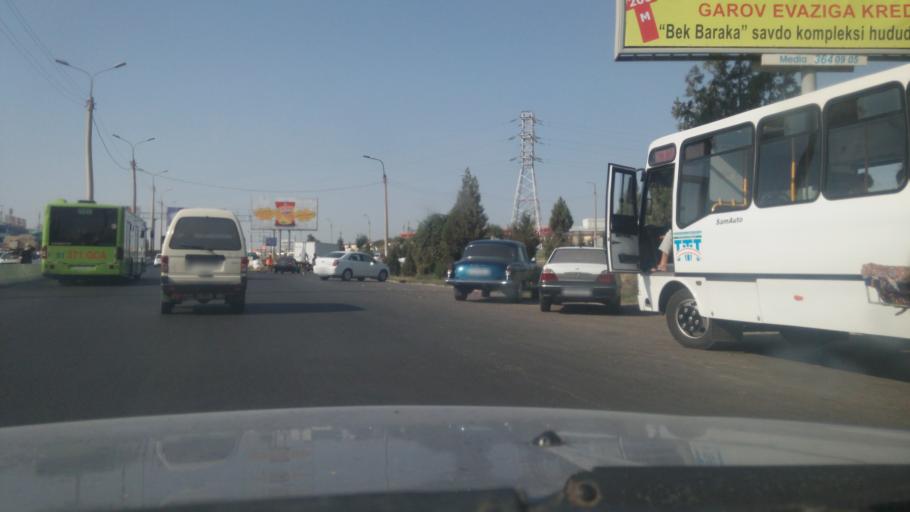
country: UZ
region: Toshkent Shahri
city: Tashkent
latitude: 41.2397
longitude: 69.1674
